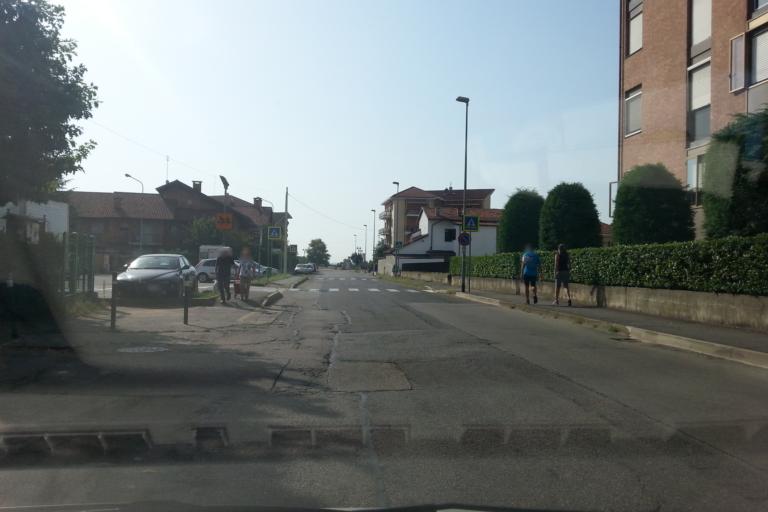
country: IT
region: Piedmont
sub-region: Provincia di Torino
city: Piossasco
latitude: 44.9912
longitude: 7.4779
